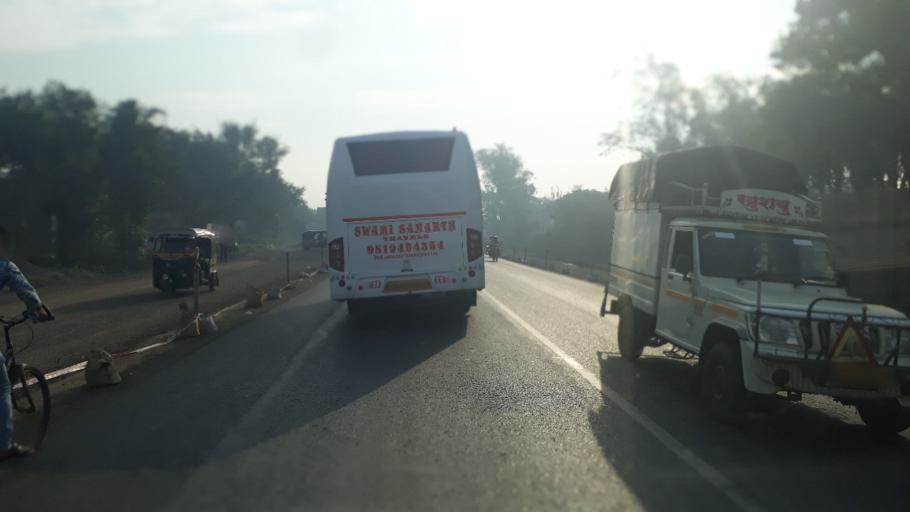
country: IN
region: Maharashtra
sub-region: Raigarh
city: Kalundri
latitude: 18.9738
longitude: 73.1266
